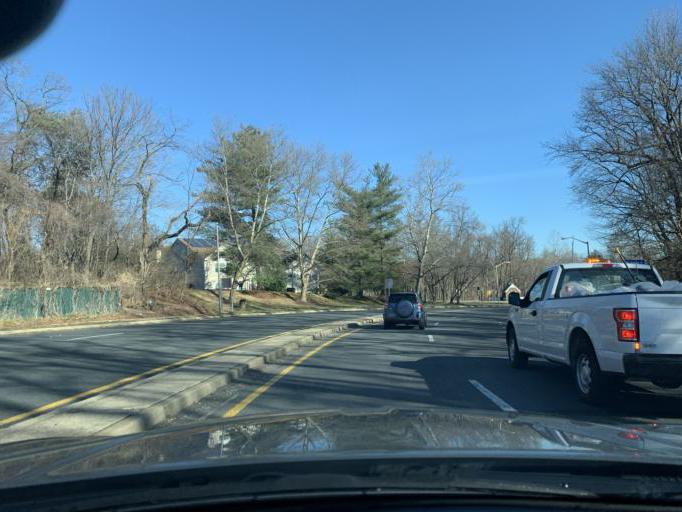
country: US
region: Maryland
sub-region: Prince George's County
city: Largo
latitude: 38.8914
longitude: -76.8535
